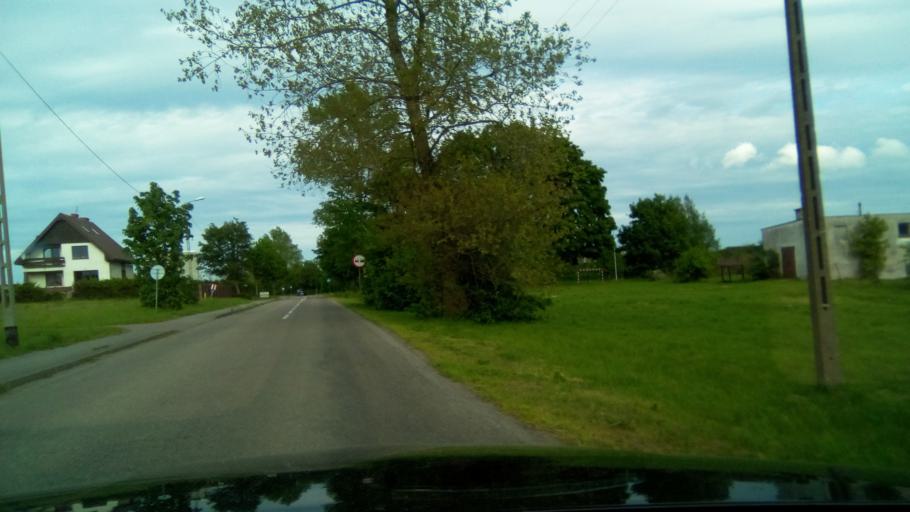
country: PL
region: Pomeranian Voivodeship
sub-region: Powiat pucki
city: Krokowa
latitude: 54.8091
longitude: 18.1890
